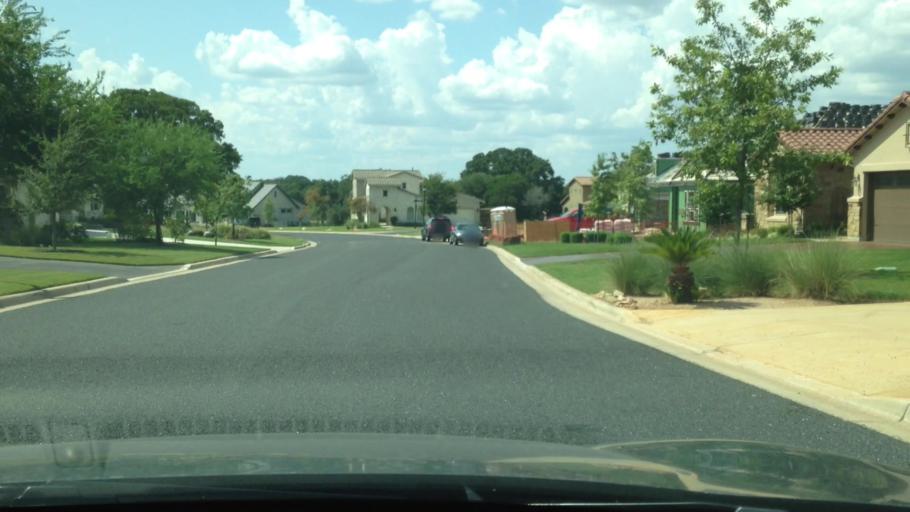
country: US
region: Texas
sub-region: Williamson County
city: Leander
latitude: 30.6375
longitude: -97.7886
